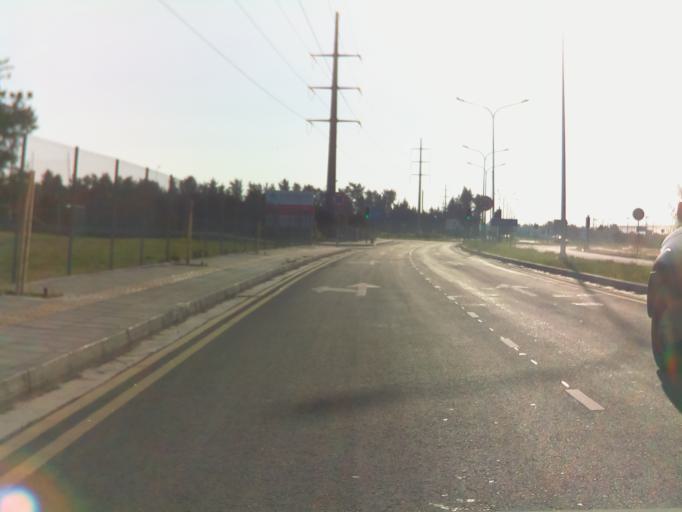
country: CY
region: Pafos
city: Paphos
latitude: 34.7443
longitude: 32.4437
